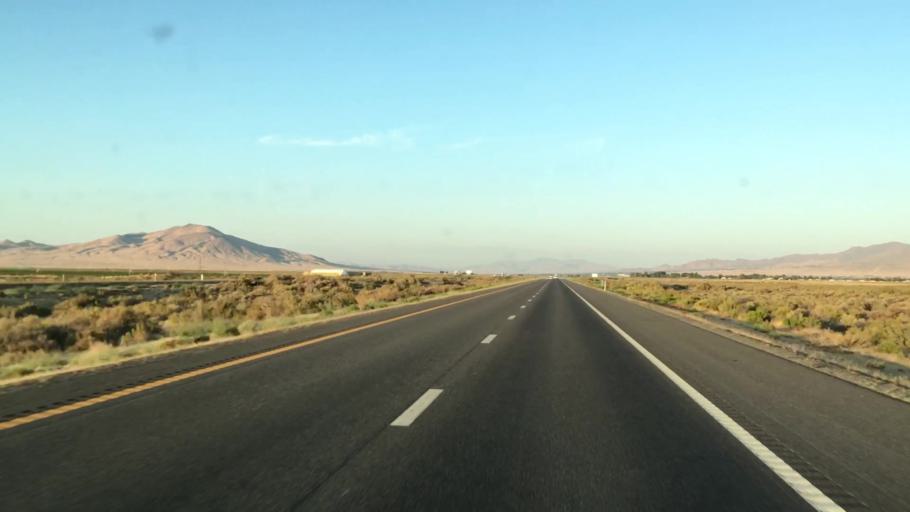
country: US
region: Nevada
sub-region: Humboldt County
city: Winnemucca
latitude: 40.9032
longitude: -117.8745
